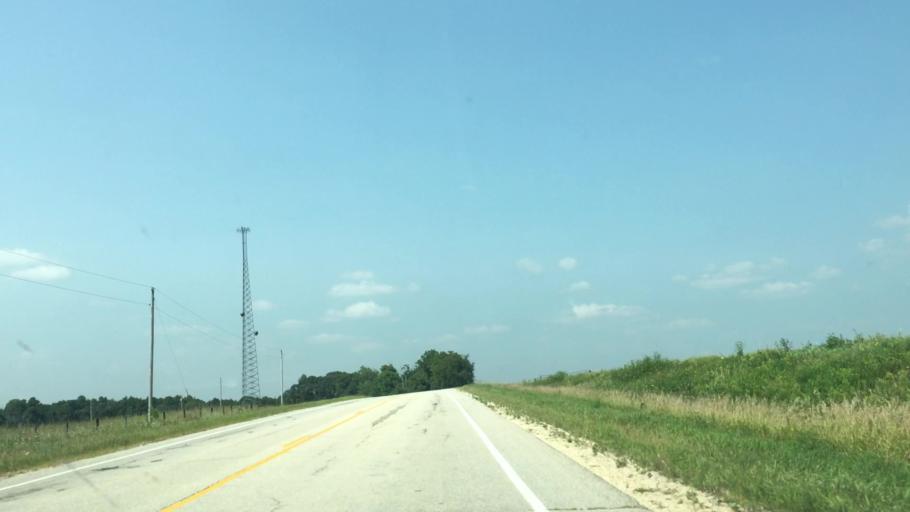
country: US
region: Minnesota
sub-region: Fillmore County
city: Harmony
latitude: 43.6631
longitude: -91.9301
